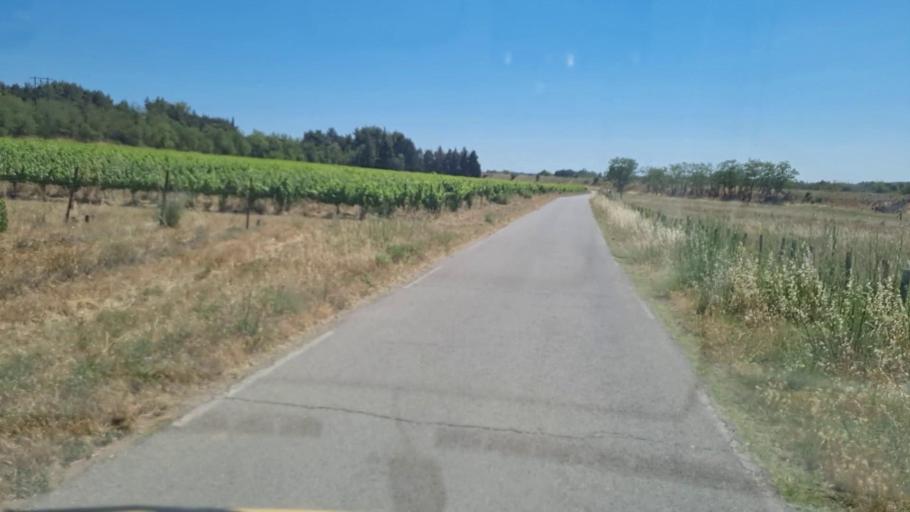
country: FR
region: Languedoc-Roussillon
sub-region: Departement du Gard
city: Vauvert
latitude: 43.6714
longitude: 4.2633
